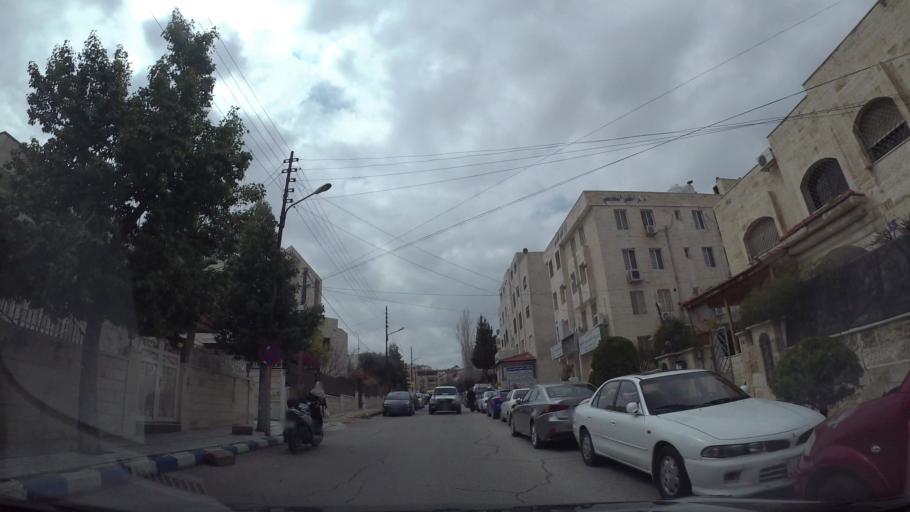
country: JO
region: Amman
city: Amman
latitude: 31.9781
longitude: 35.9005
